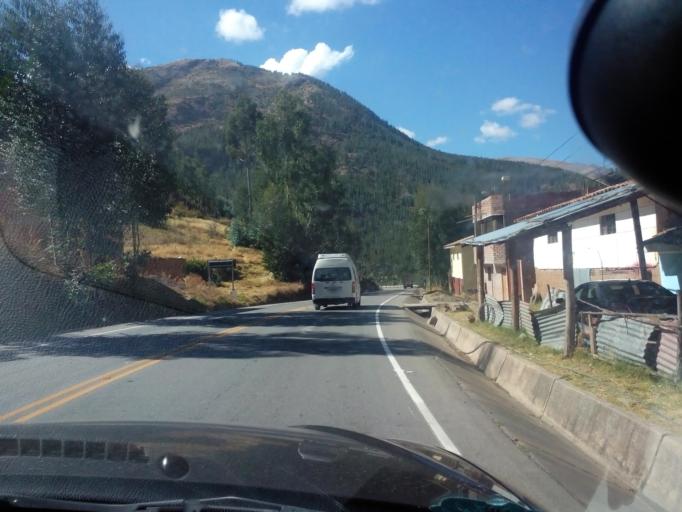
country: PE
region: Cusco
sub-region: Provincia de Quispicanchis
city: Urcos
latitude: -13.6873
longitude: -71.5984
